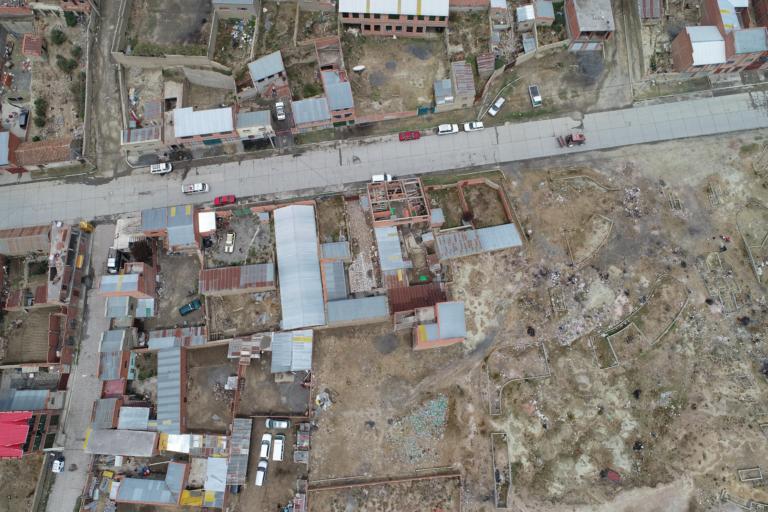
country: BO
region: La Paz
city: Achacachi
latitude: -16.0509
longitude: -68.6825
